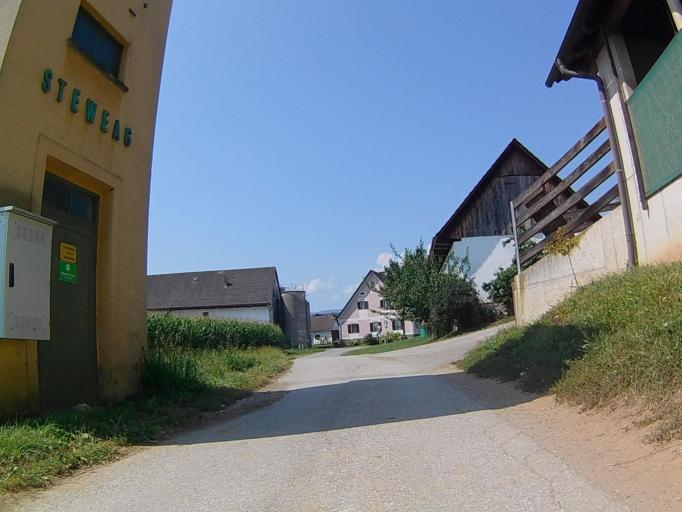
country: AT
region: Styria
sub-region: Politischer Bezirk Deutschlandsberg
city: Pitschgau
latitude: 46.7028
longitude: 15.2885
